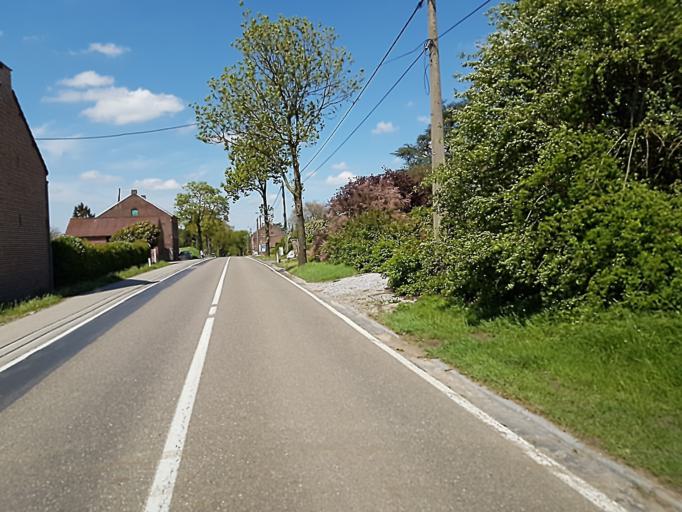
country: BE
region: Flanders
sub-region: Provincie Vlaams-Brabant
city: Tienen
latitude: 50.8281
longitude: 4.9228
